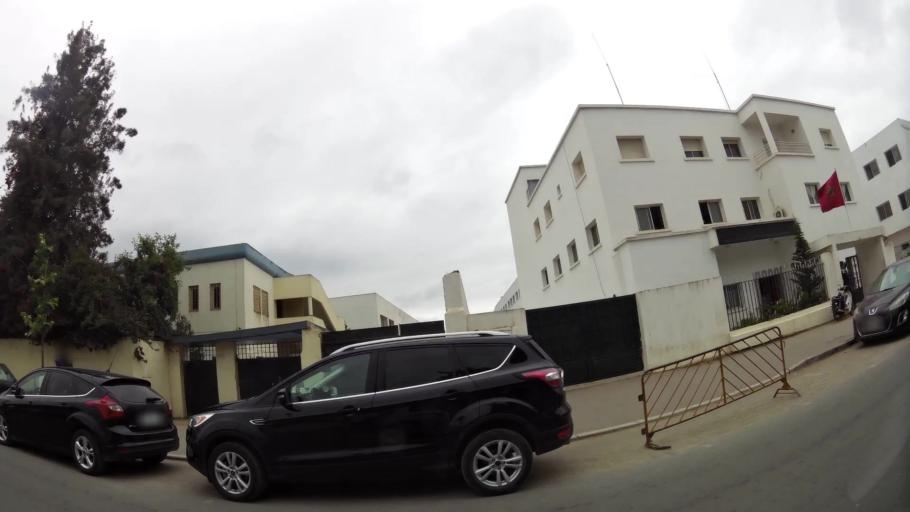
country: MA
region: Rabat-Sale-Zemmour-Zaer
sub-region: Rabat
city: Rabat
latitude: 33.9752
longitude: -6.8184
